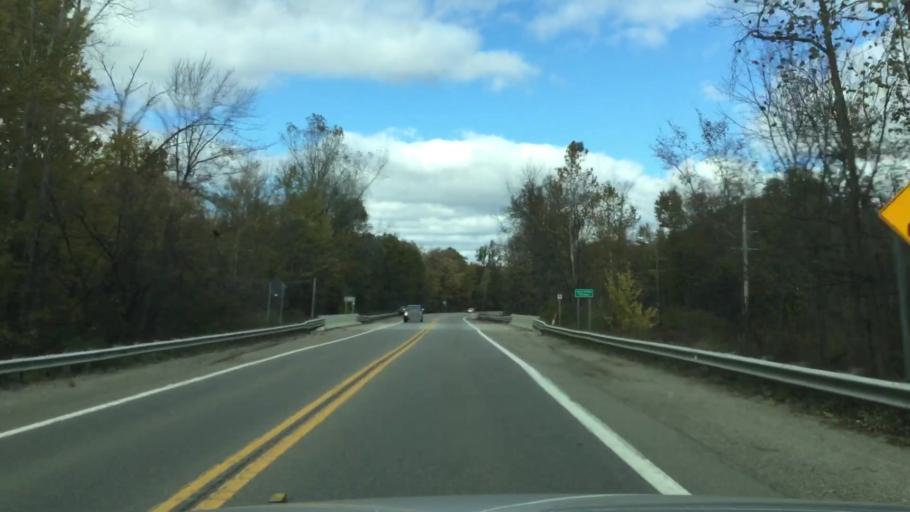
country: US
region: Michigan
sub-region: Lapeer County
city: Barnes Lake-Millers Lake
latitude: 43.2105
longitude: -83.3140
